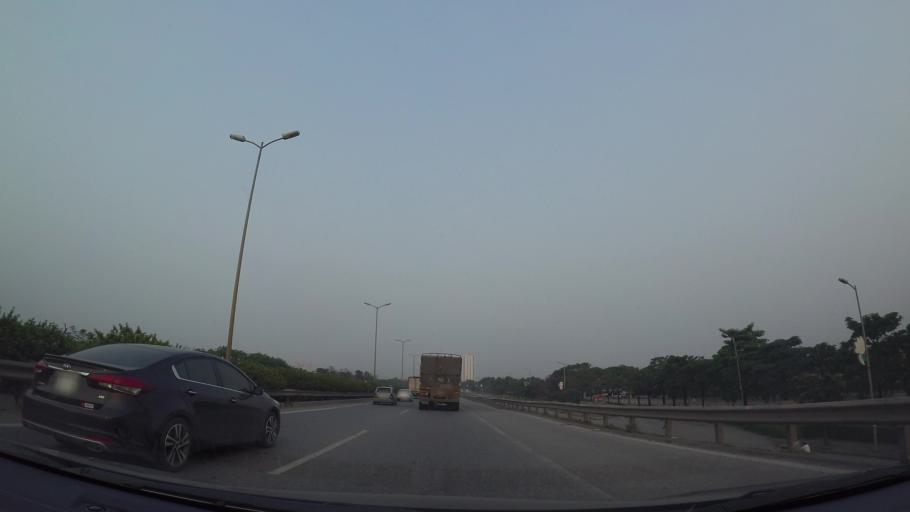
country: VN
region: Ha Noi
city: Van Dien
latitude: 20.9653
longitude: 105.8529
